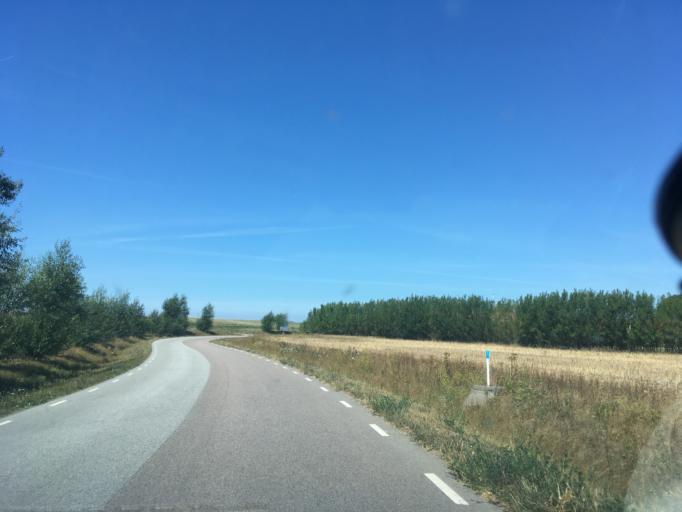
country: SE
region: Skane
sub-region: Trelleborgs Kommun
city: Skare
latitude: 55.3855
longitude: 13.0839
